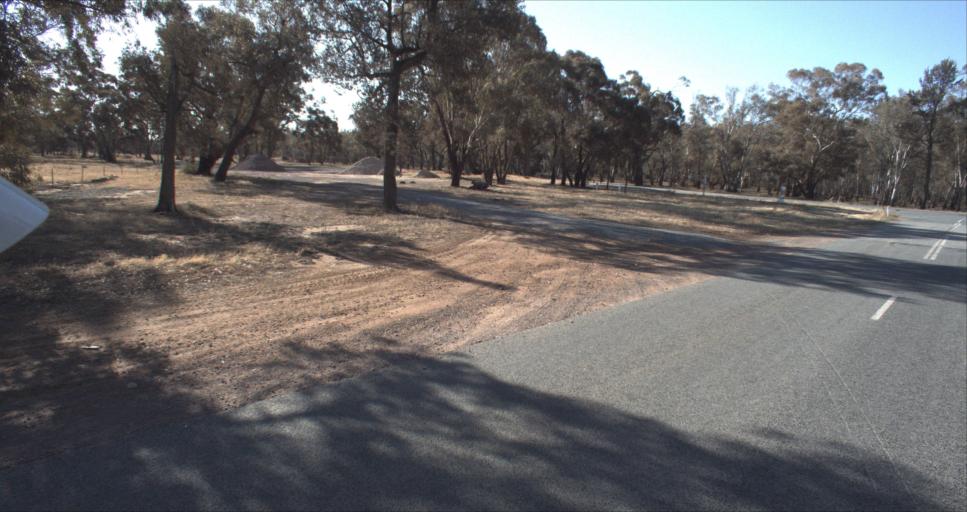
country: AU
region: New South Wales
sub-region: Leeton
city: Leeton
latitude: -34.6438
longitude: 146.3526
